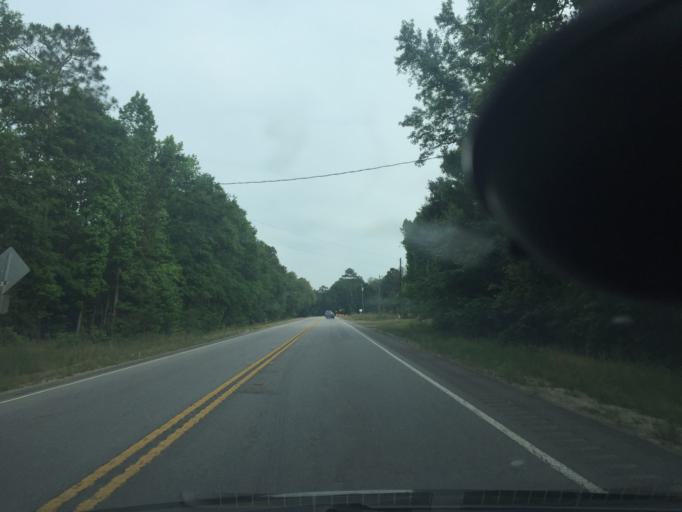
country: US
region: Georgia
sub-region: Bryan County
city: Richmond Hill
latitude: 32.0131
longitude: -81.2971
